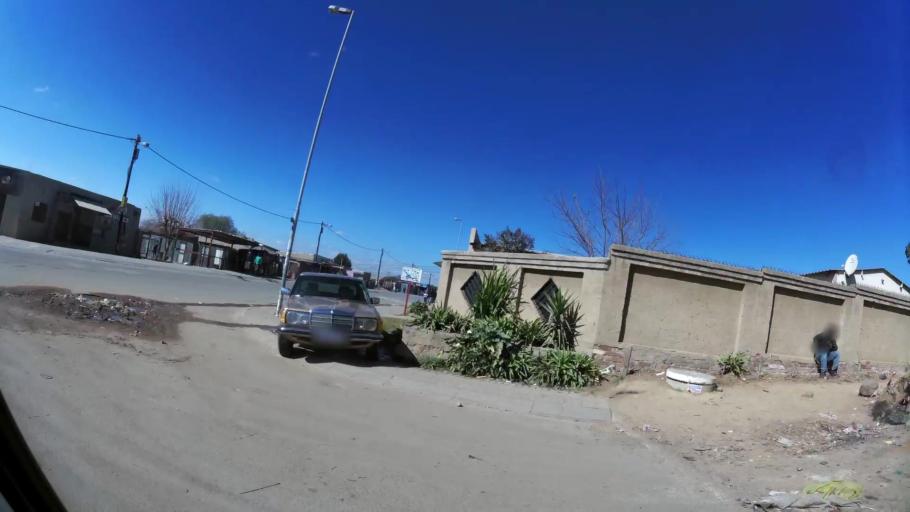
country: ZA
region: Gauteng
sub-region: City of Johannesburg Metropolitan Municipality
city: Midrand
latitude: -25.9191
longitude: 28.0908
